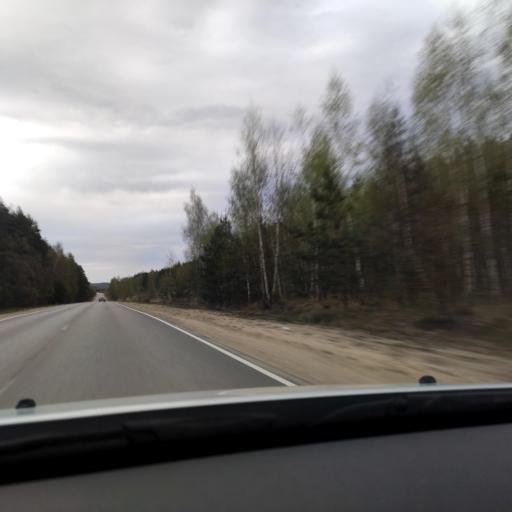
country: RU
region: Lipetsk
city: Zadonsk
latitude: 52.4287
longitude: 38.9571
